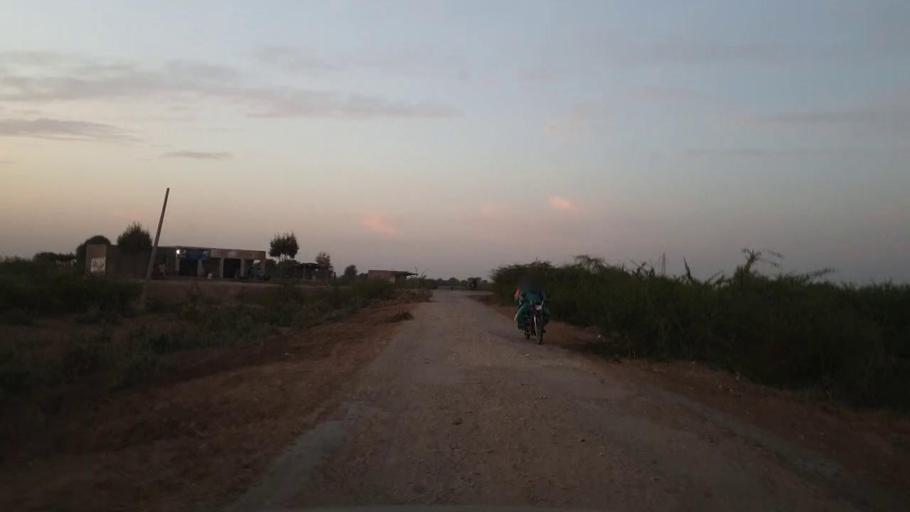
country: PK
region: Sindh
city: Kunri
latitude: 25.1535
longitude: 69.5535
